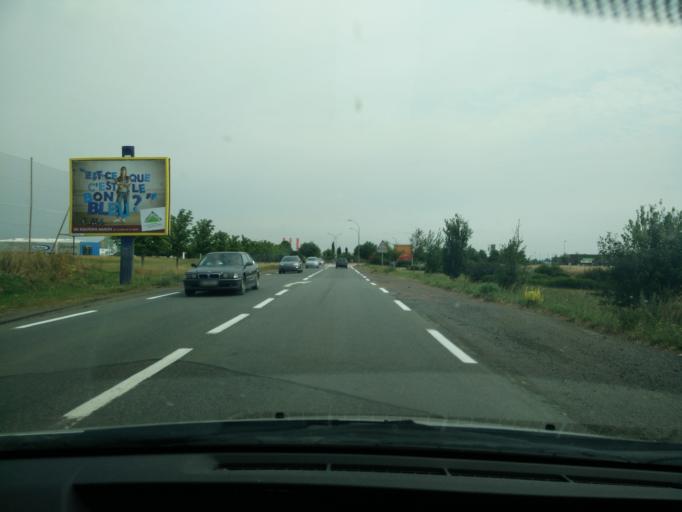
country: FR
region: Poitou-Charentes
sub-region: Departement des Deux-Sevres
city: Thouars
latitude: 46.9882
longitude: -0.1972
